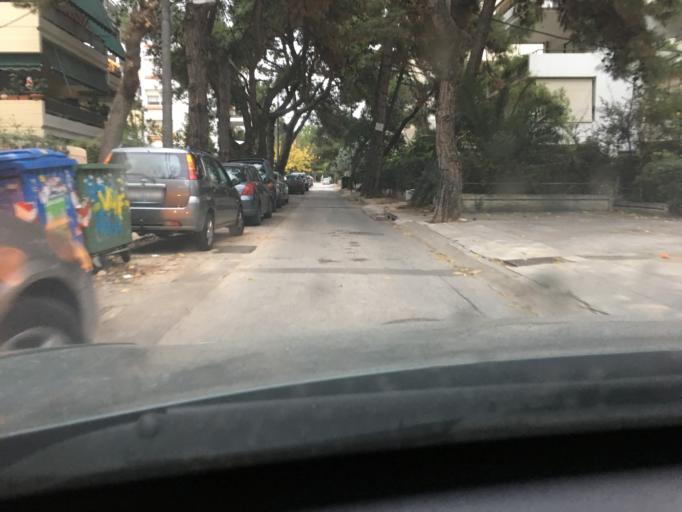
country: GR
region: Attica
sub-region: Nomarchia Athinas
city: Vrilissia
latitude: 38.0304
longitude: 23.8272
